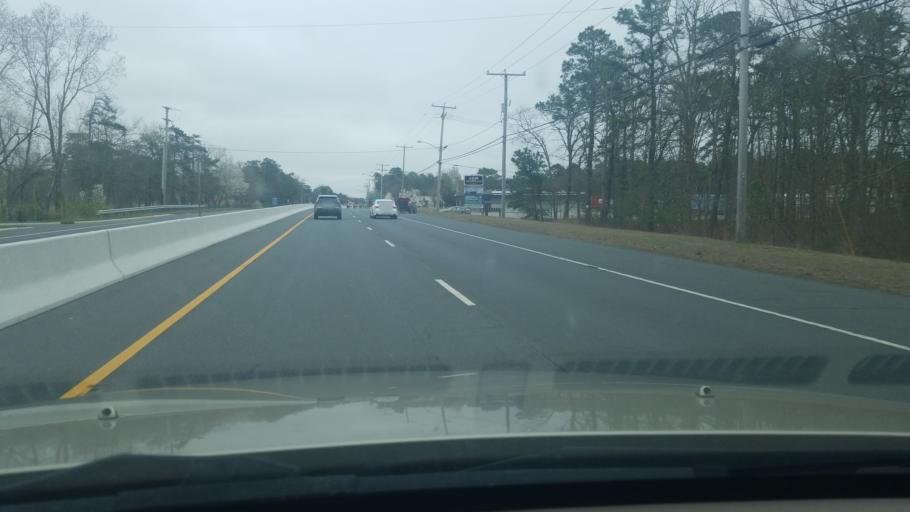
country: US
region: New Jersey
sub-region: Ocean County
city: Leisure Village West-Pine Lake Park
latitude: 39.9927
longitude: -74.2719
